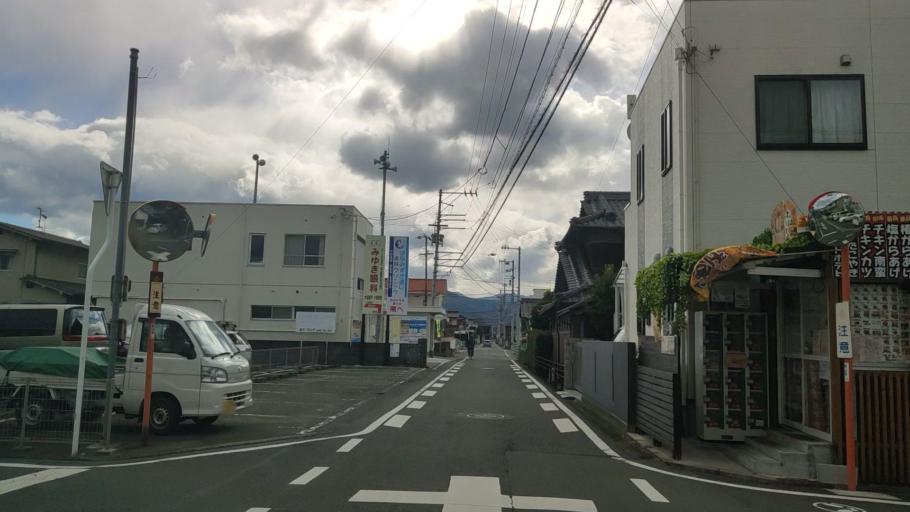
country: JP
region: Ehime
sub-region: Shikoku-chuo Shi
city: Matsuyama
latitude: 33.8121
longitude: 132.7525
